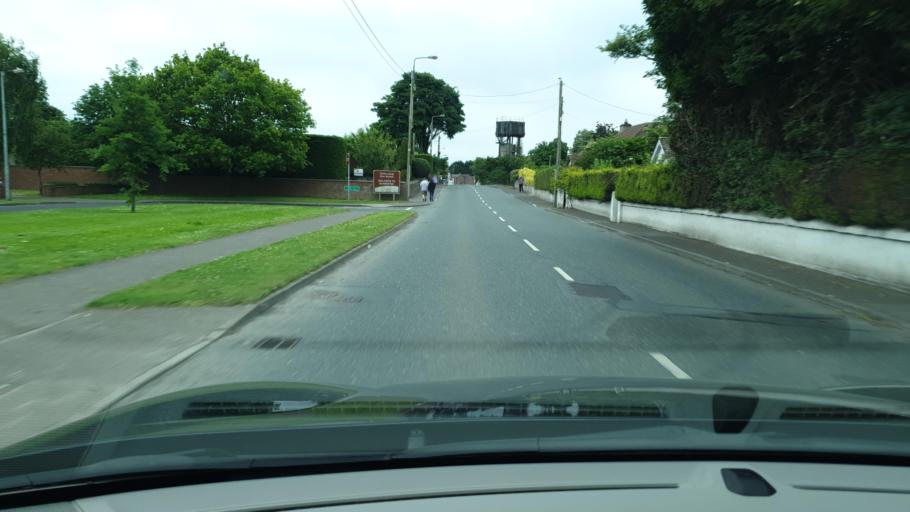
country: IE
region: Leinster
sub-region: An Mhi
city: Dunboyne
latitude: 53.4239
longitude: -6.4729
